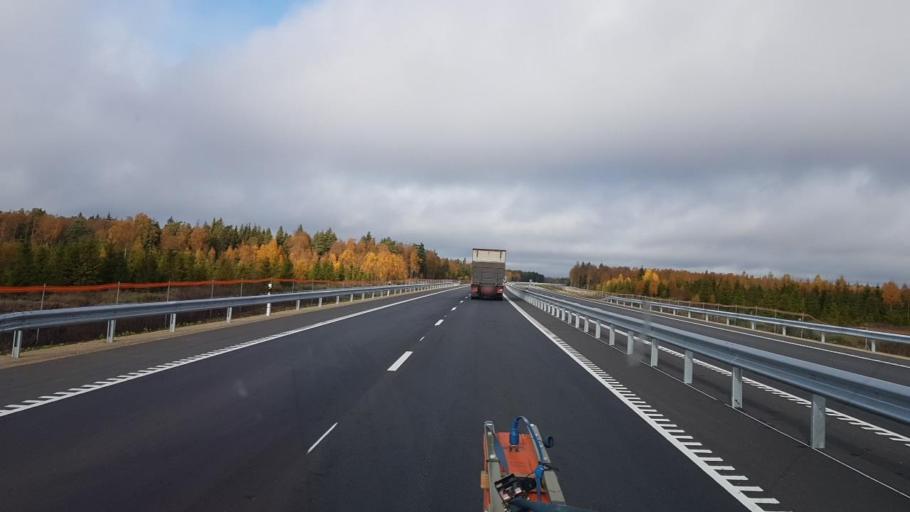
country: EE
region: Jaervamaa
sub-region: Paide linn
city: Paide
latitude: 59.0101
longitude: 25.5600
